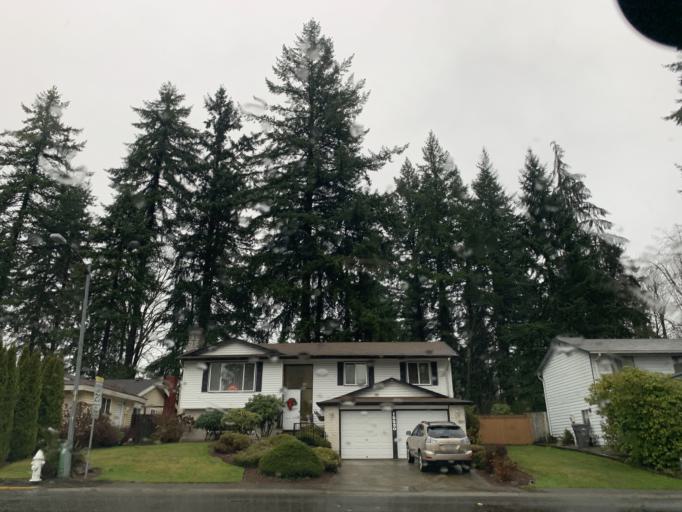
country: US
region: Washington
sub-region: King County
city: Kingsgate
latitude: 47.7406
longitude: -122.1815
